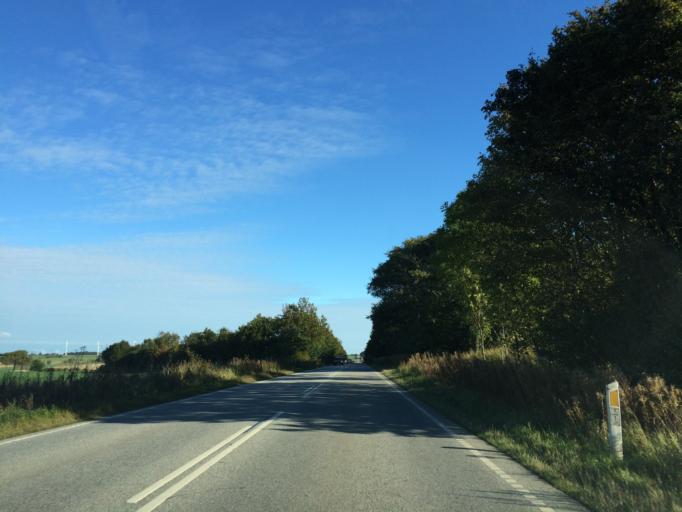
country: DK
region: Central Jutland
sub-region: Randers Kommune
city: Randers
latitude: 56.4061
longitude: 10.0011
